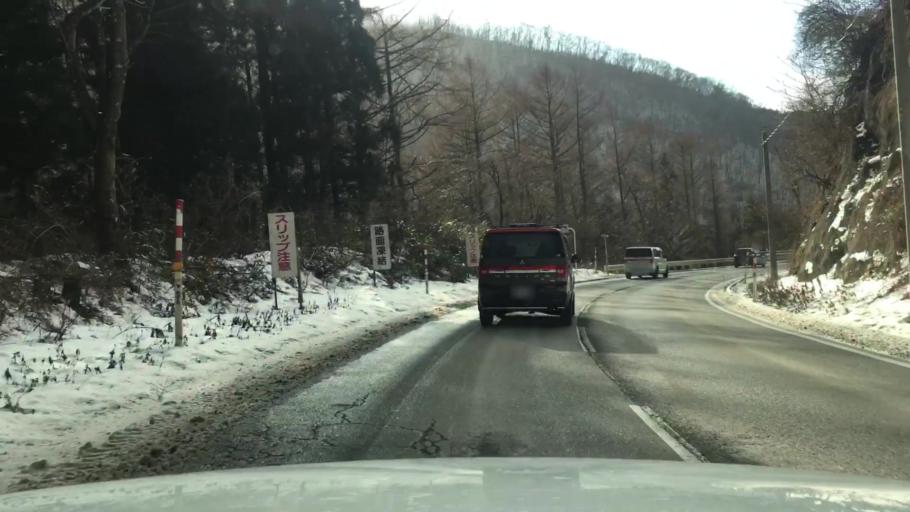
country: JP
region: Iwate
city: Morioka-shi
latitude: 39.6658
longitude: 141.3159
